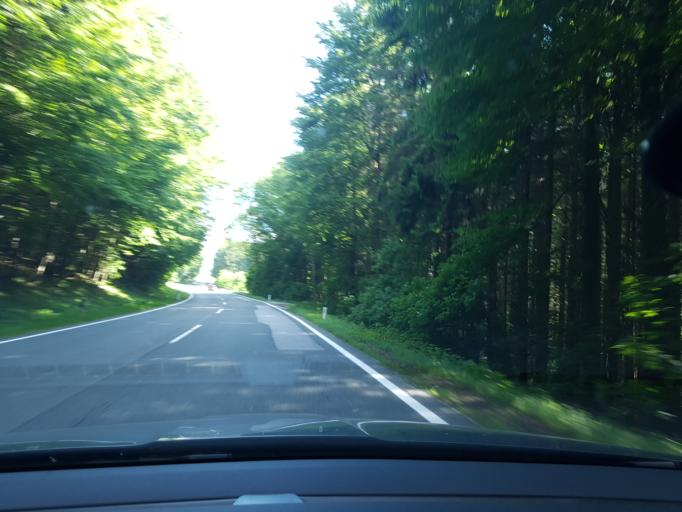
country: AT
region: Salzburg
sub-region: Politischer Bezirk Salzburg-Umgebung
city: Obertrum am See
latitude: 47.9156
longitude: 13.0827
